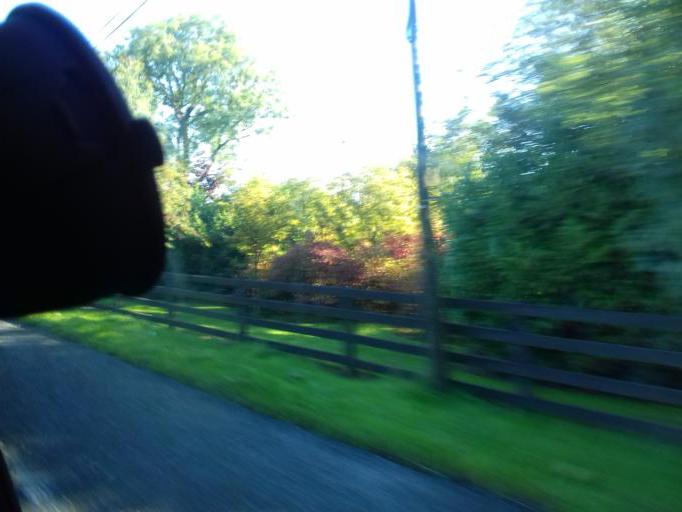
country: IE
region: Leinster
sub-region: An Iarmhi
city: Kilbeggan
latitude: 53.3321
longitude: -7.5116
